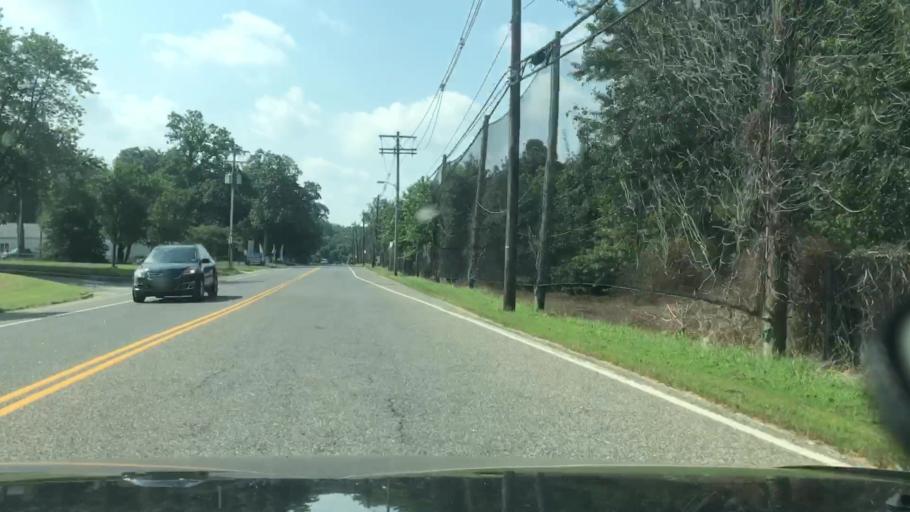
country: US
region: New Jersey
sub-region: Ocean County
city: Toms River
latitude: 39.9872
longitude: -74.1858
